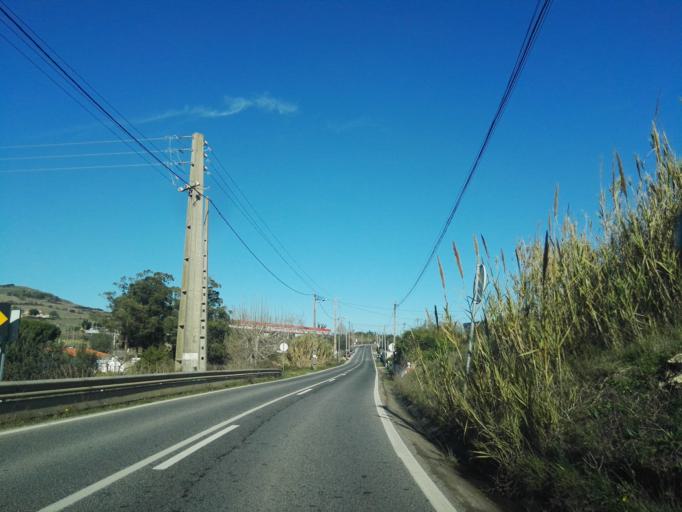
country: PT
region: Lisbon
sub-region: Mafra
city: Venda do Pinheiro
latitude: 38.8904
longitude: -9.1889
